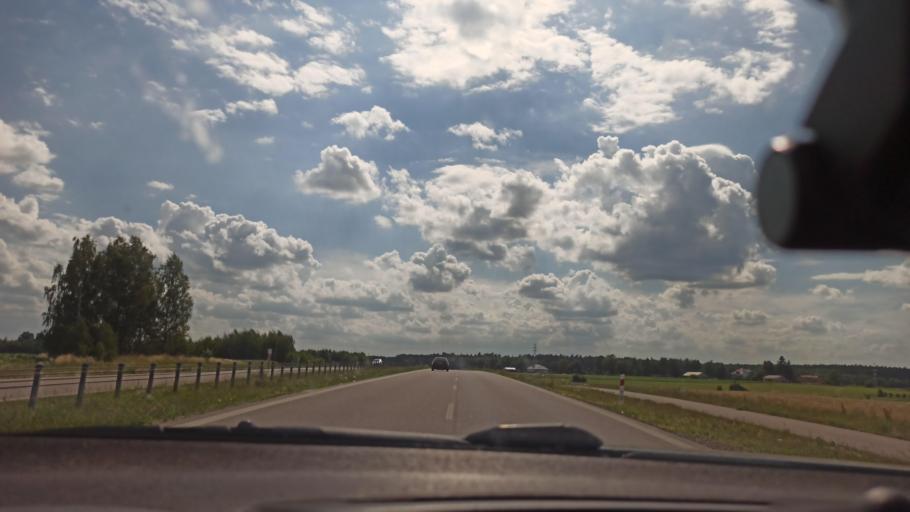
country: PL
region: Podlasie
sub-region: Powiat bialostocki
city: Turosn Koscielna
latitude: 53.0447
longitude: 23.0352
